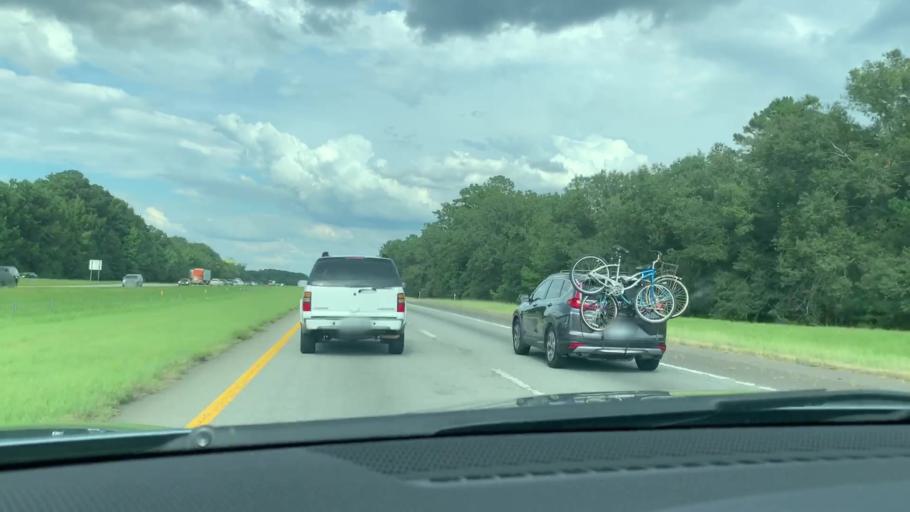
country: US
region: South Carolina
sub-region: Jasper County
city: Ridgeland
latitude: 32.5806
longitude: -80.9292
